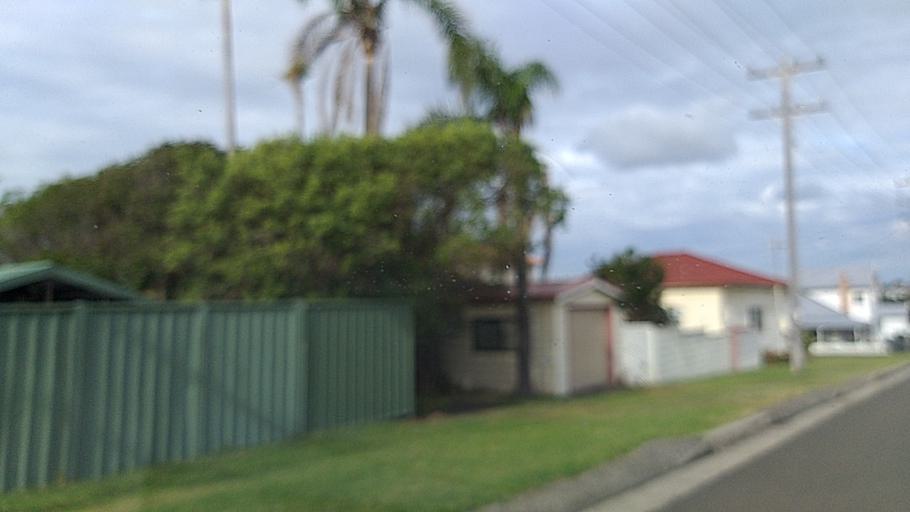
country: AU
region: New South Wales
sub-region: Wollongong
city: Bulli
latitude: -34.3214
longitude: 150.9243
